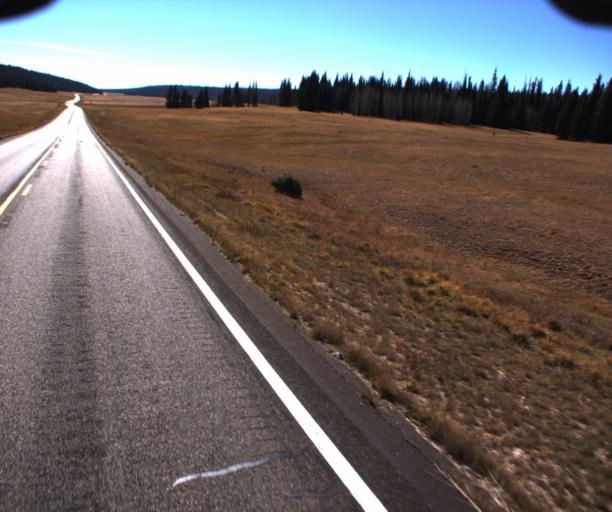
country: US
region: Arizona
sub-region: Coconino County
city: Grand Canyon
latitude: 36.4090
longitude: -112.1313
